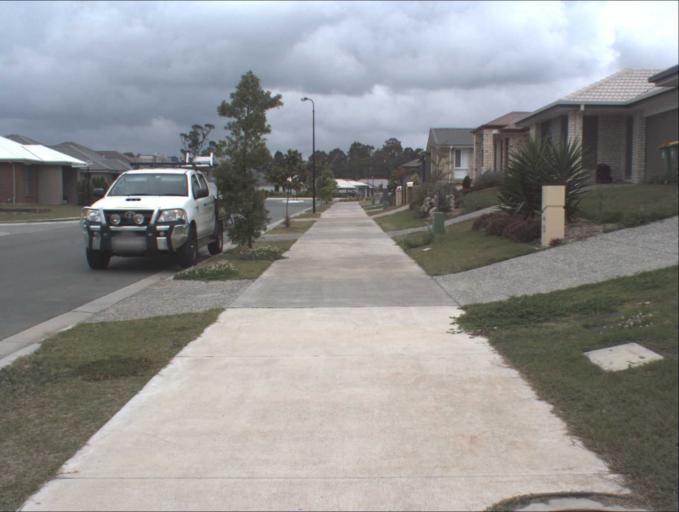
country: AU
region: Queensland
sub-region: Logan
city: Logan Reserve
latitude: -27.7104
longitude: 153.1115
